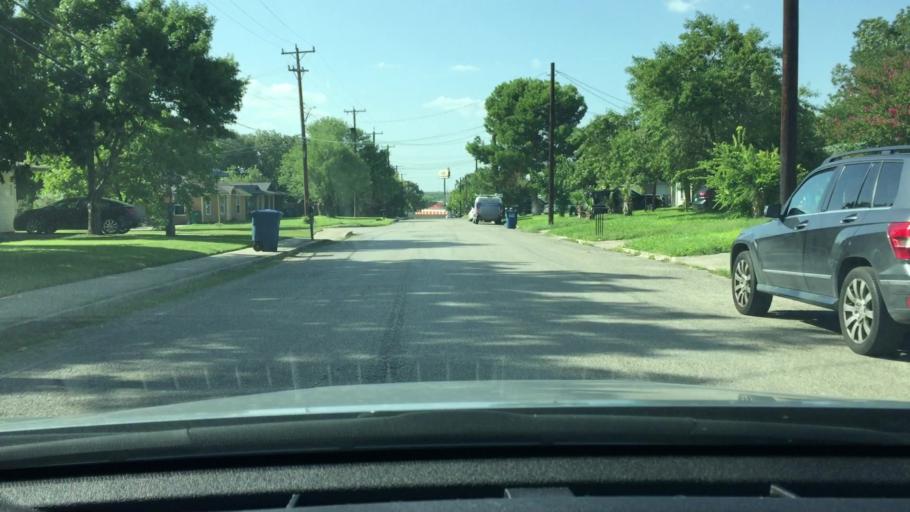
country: US
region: Texas
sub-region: Bexar County
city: Windcrest
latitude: 29.5322
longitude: -98.3840
